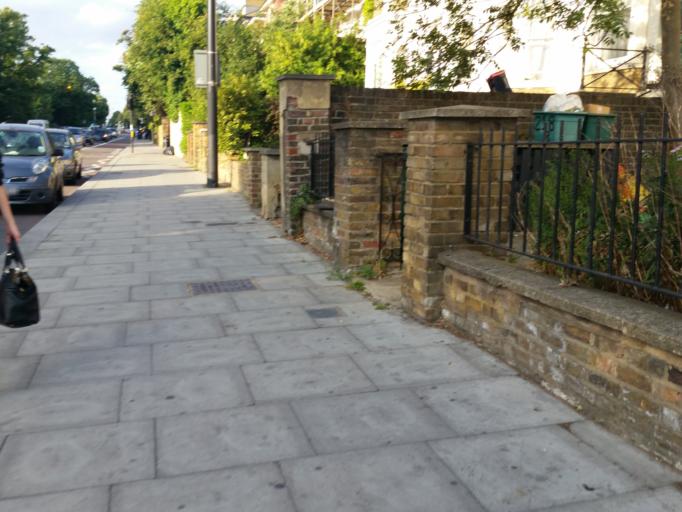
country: GB
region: England
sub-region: Greater London
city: Holloway
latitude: 51.5461
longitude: -0.1327
